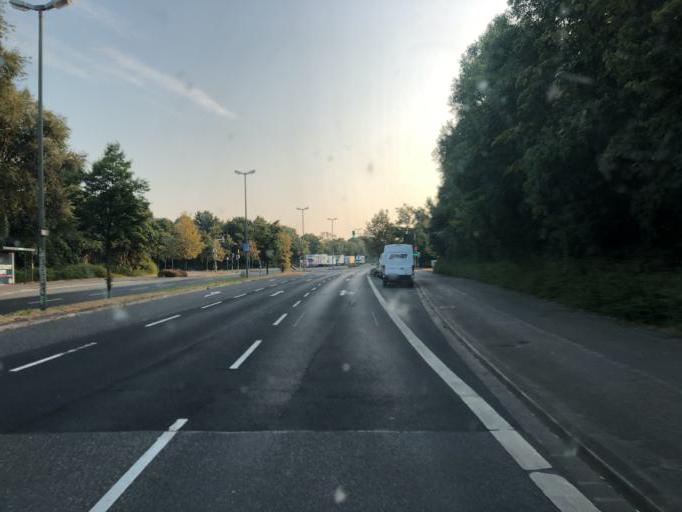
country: DE
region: North Rhine-Westphalia
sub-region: Regierungsbezirk Dusseldorf
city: Neuss
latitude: 51.1995
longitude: 6.6653
